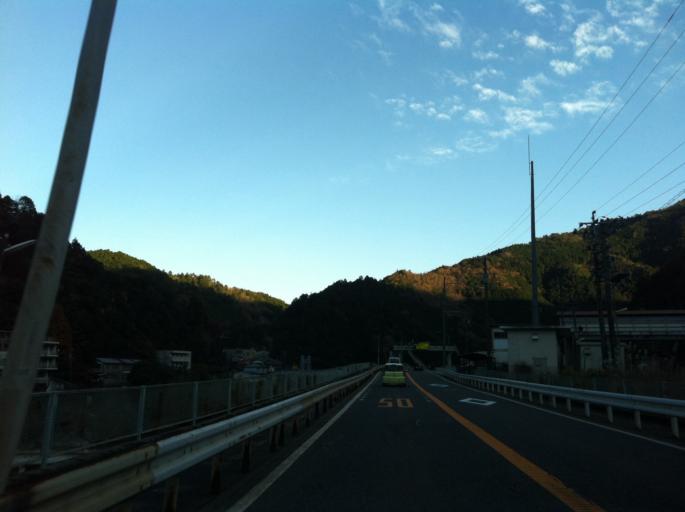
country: JP
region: Gifu
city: Mitake
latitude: 35.5805
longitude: 137.1833
